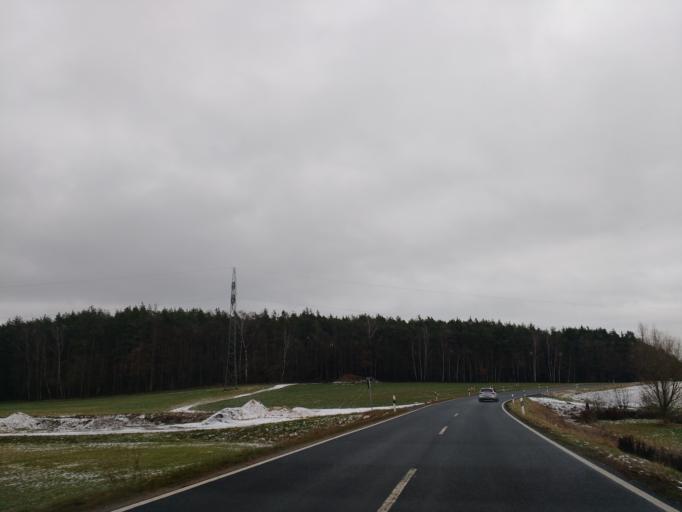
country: DE
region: Bavaria
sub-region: Regierungsbezirk Mittelfranken
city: Weisendorf
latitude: 49.6095
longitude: 10.8341
